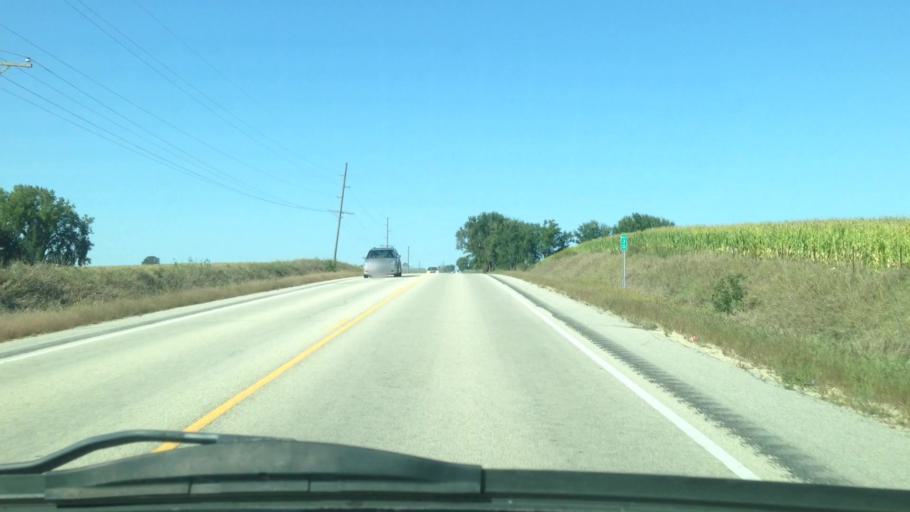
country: US
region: Minnesota
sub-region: Fillmore County
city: Rushford
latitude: 43.9060
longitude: -91.7401
